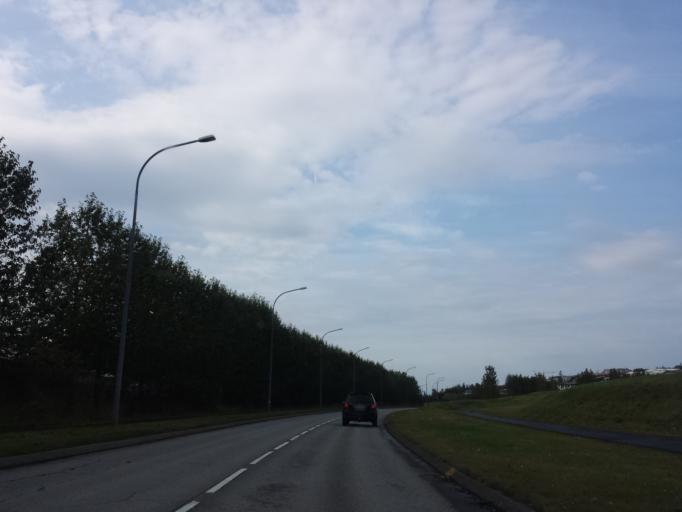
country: IS
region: Capital Region
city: Reykjavik
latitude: 64.1062
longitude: -21.8598
